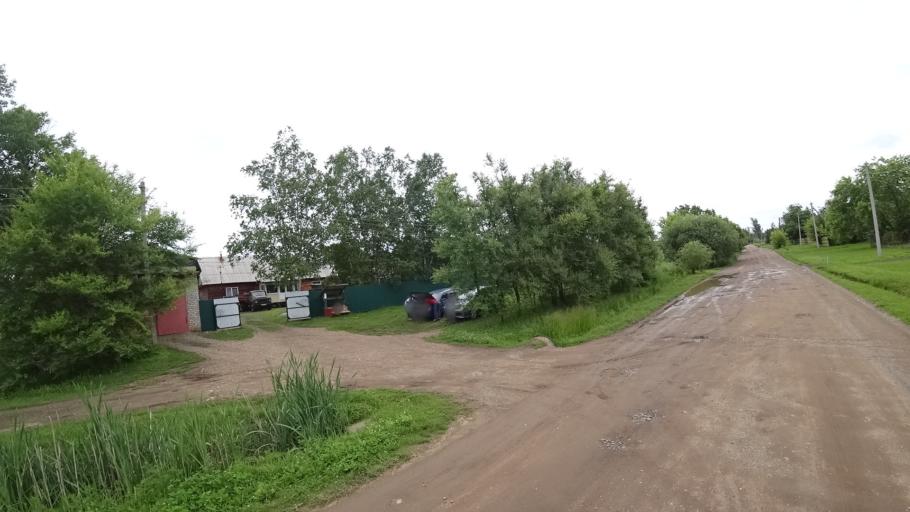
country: RU
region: Primorskiy
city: Novosysoyevka
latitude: 44.2507
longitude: 133.3762
